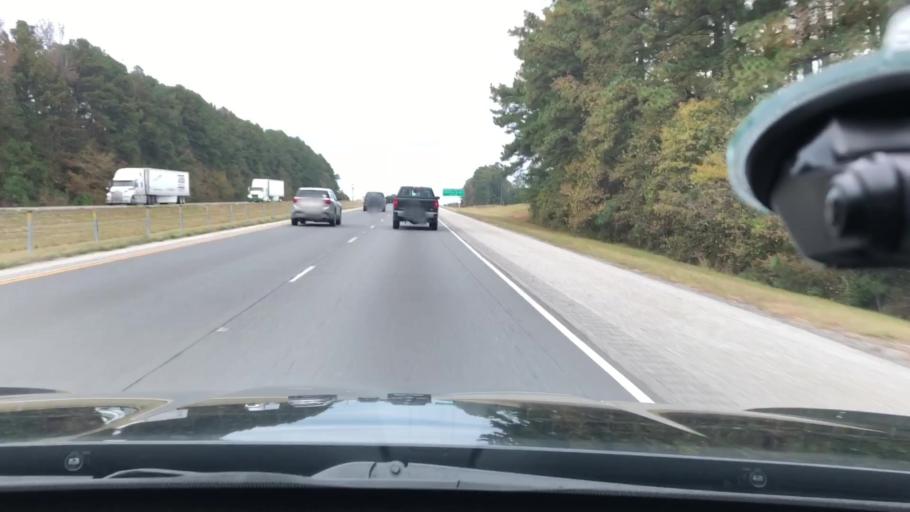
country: US
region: Arkansas
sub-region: Clark County
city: Arkadelphia
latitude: 34.1088
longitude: -93.0980
